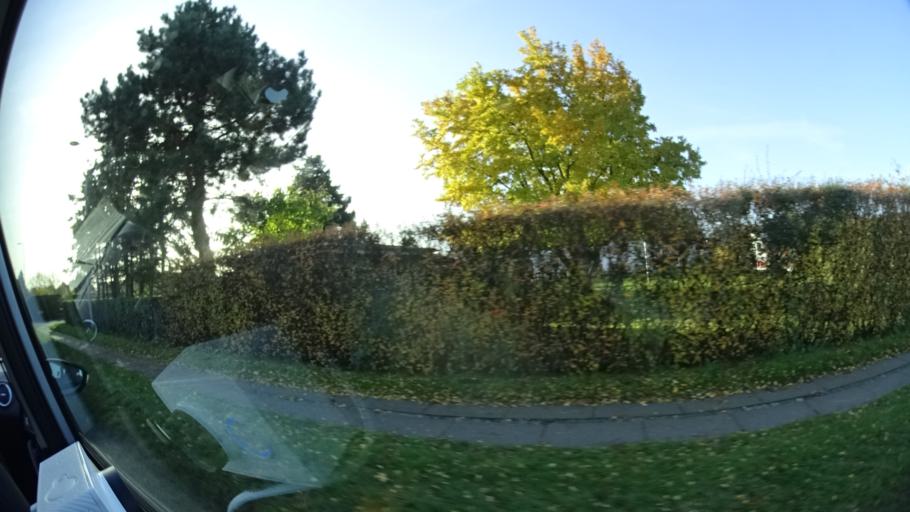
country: DK
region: South Denmark
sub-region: Odense Kommune
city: Hojby
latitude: 55.3402
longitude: 10.4326
